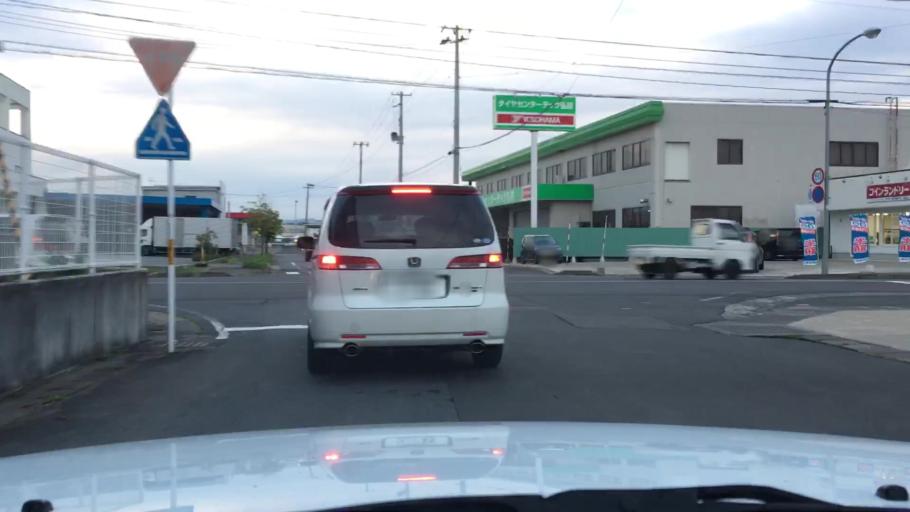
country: JP
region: Aomori
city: Hirosaki
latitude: 40.5989
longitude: 140.5077
